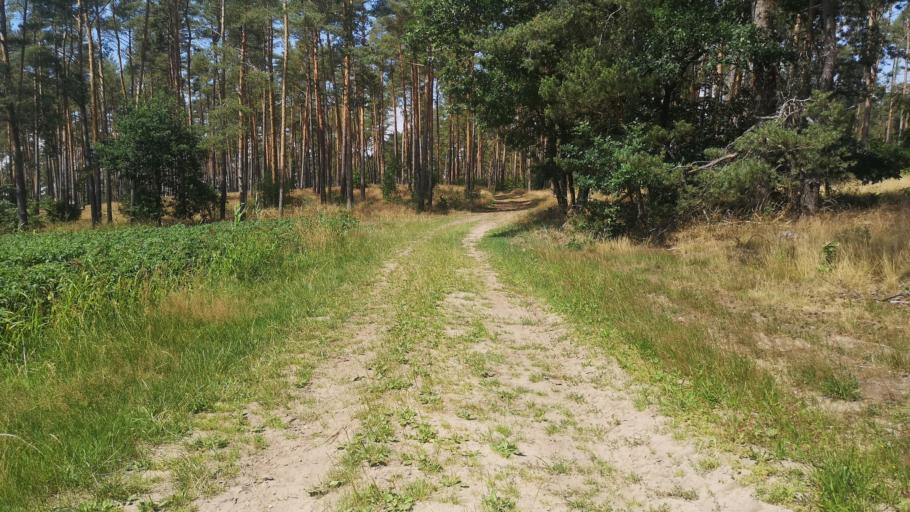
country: DE
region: Lower Saxony
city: Dahlem
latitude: 53.2237
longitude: 10.7290
